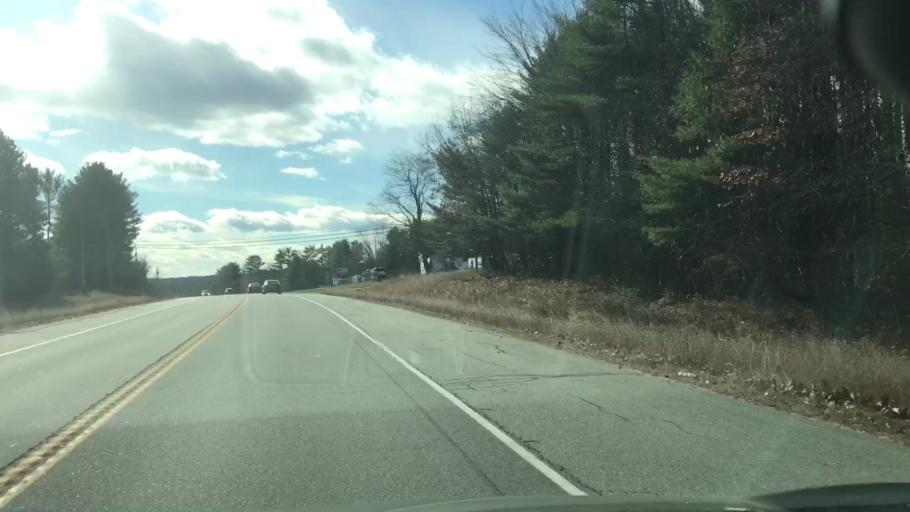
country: US
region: New Hampshire
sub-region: Merrimack County
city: Pittsfield
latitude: 43.2865
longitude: -71.3597
